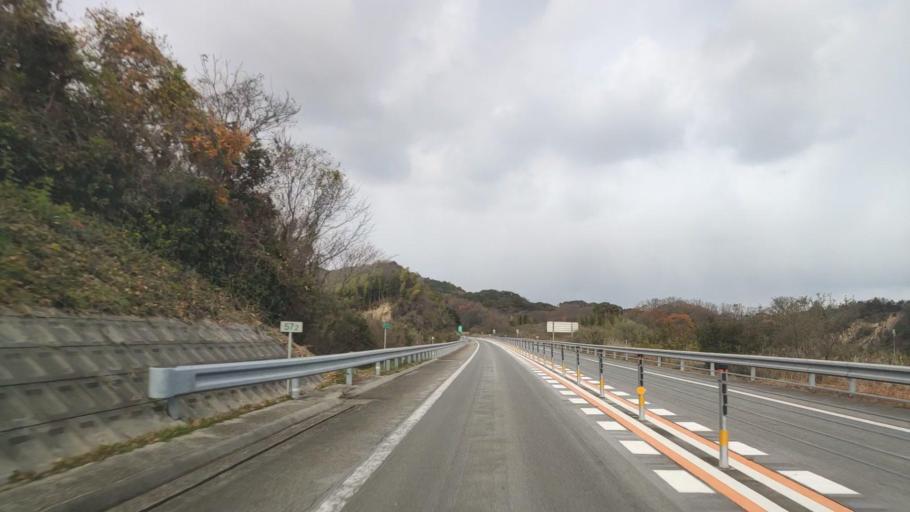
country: JP
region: Ehime
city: Hojo
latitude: 34.0712
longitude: 132.9747
